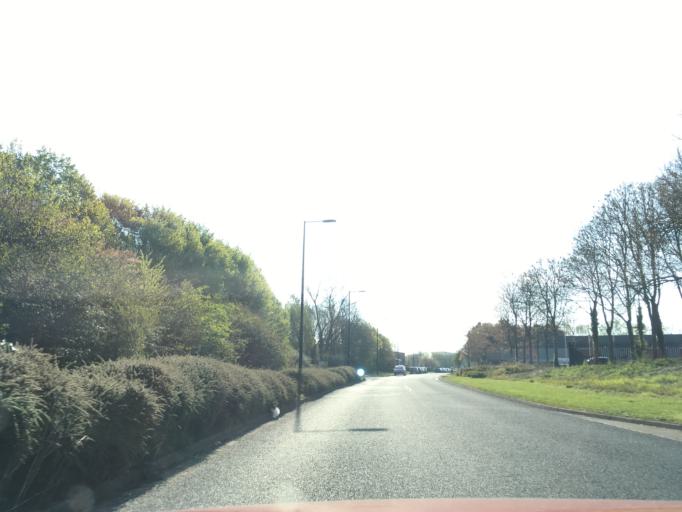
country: GB
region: England
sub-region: Milton Keynes
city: Newport Pagnell
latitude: 52.0694
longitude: -0.7328
